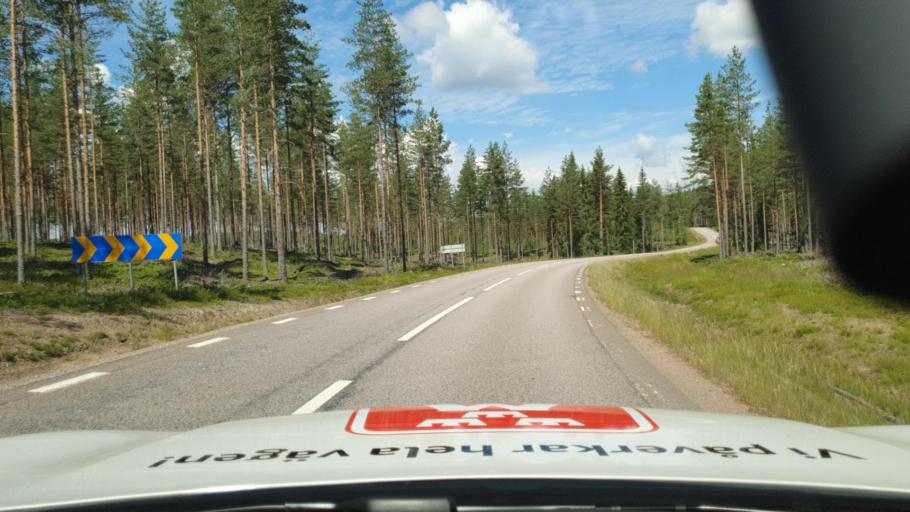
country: SE
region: Vaermland
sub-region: Torsby Kommun
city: Torsby
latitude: 60.3732
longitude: 12.9228
